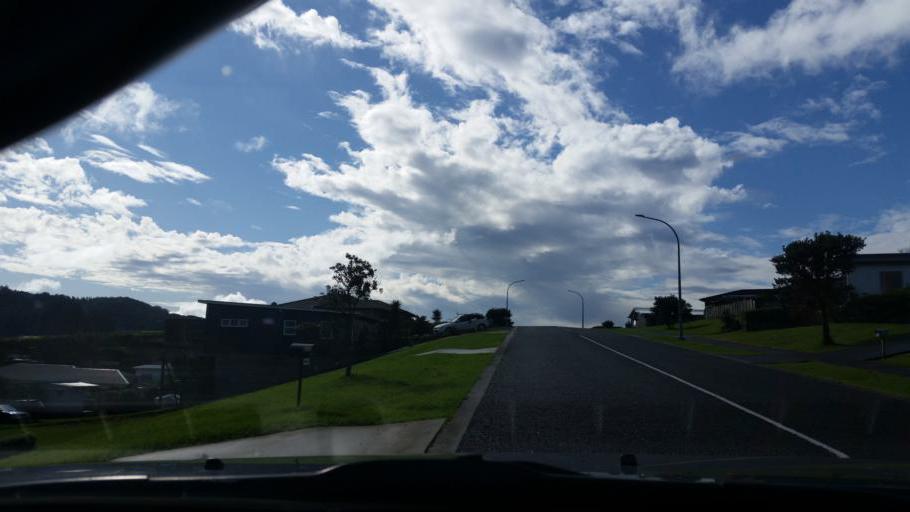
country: NZ
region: Auckland
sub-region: Auckland
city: Wellsford
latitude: -36.0882
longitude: 174.5765
